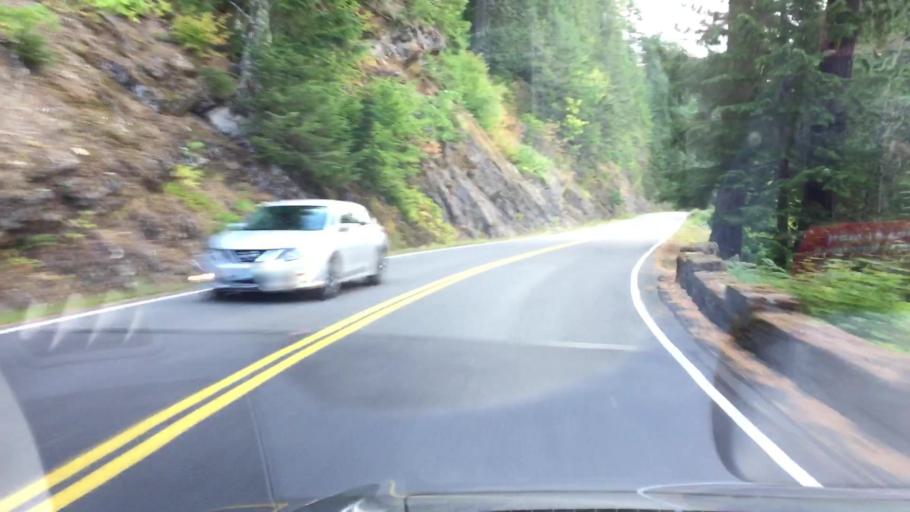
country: US
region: Washington
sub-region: Pierce County
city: Buckley
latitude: 46.7401
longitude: -121.5778
